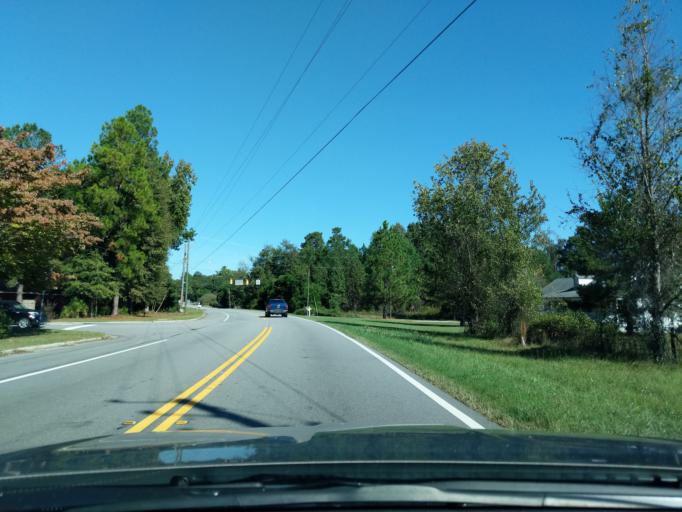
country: US
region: Georgia
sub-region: Richmond County
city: Hephzibah
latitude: 33.3569
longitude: -81.9977
